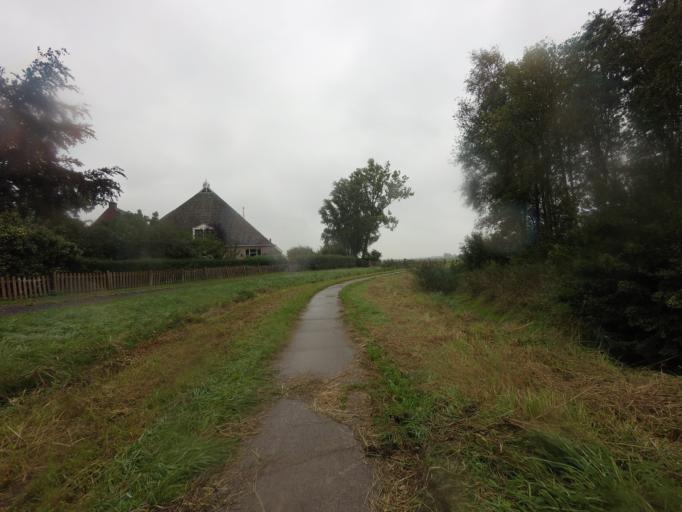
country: NL
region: Friesland
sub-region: Gemeente Boarnsterhim
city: Nes
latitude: 53.0343
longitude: 5.8691
